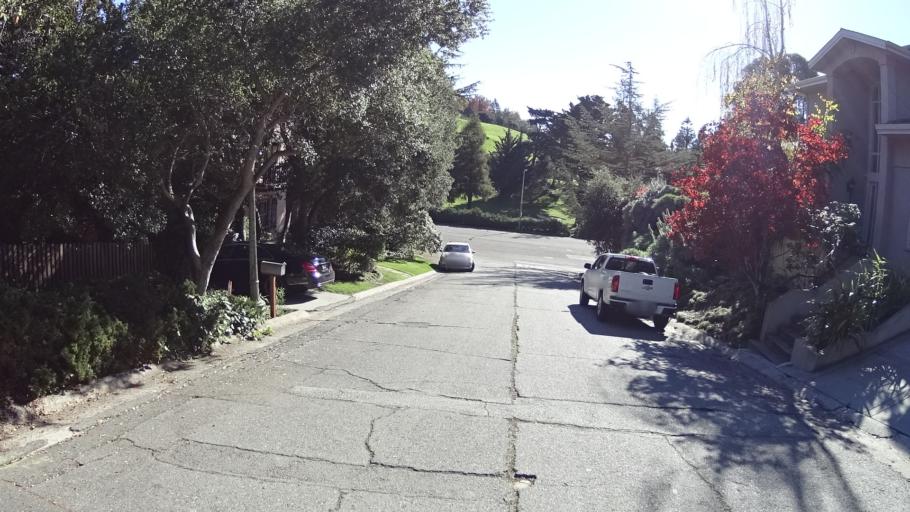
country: US
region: California
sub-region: Alameda County
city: Piedmont
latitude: 37.8416
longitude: -122.2394
